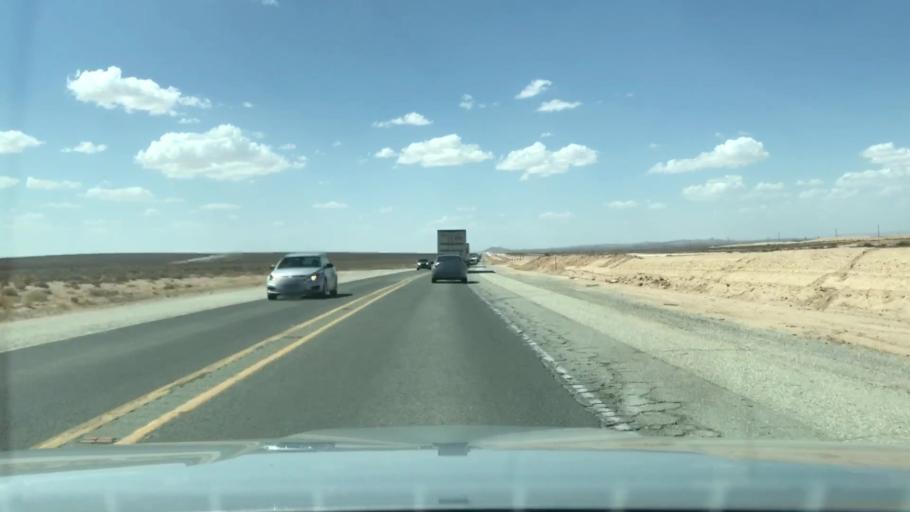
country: US
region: California
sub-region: Kern County
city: Boron
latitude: 34.9632
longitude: -117.4451
